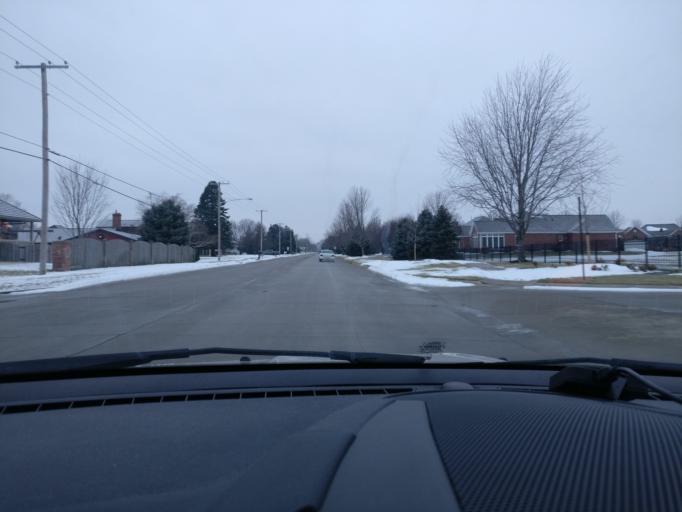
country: US
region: Nebraska
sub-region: Dodge County
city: Fremont
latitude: 41.4445
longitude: -96.4569
